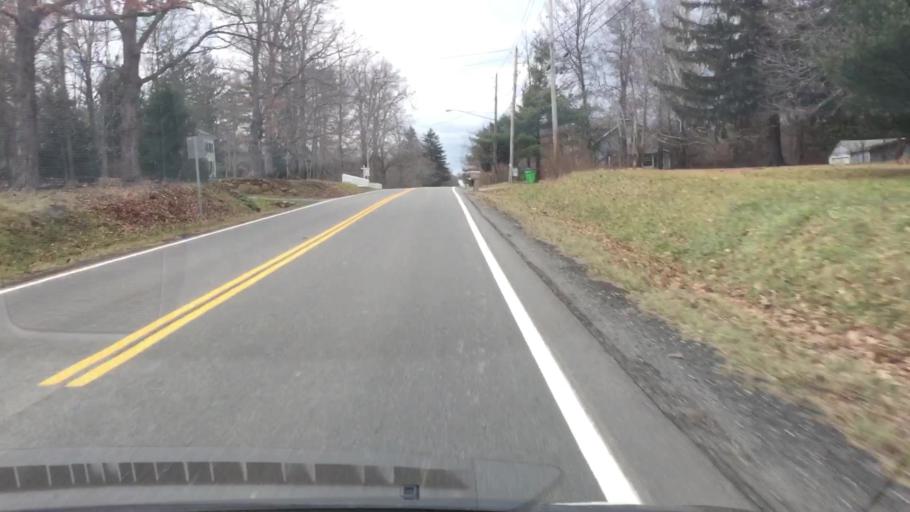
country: US
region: Ohio
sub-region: Summit County
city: Boston Heights
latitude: 41.2422
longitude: -81.5002
